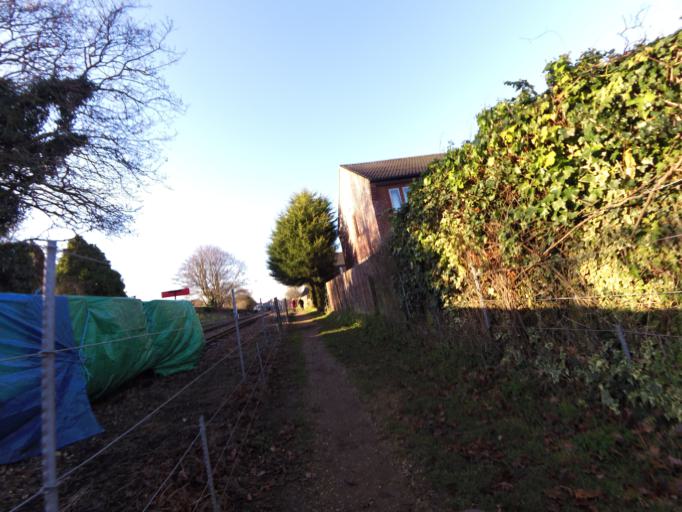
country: GB
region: England
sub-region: Norfolk
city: Aylsham
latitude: 52.7906
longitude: 1.2592
